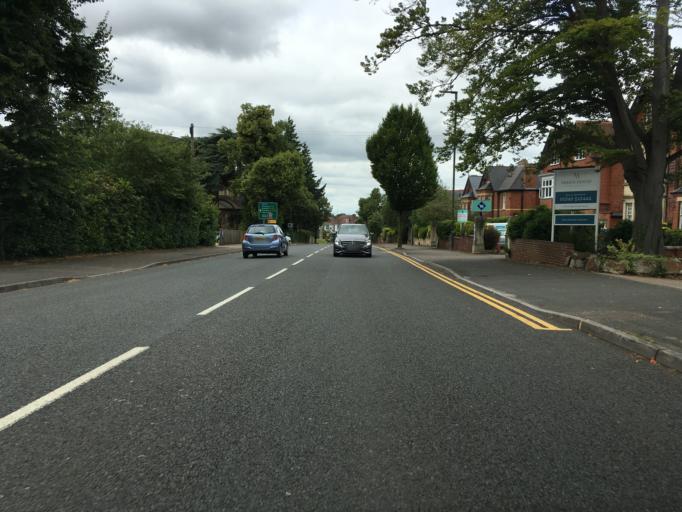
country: GB
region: England
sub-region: Gloucestershire
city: Charlton Kings
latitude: 51.8898
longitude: -2.0572
